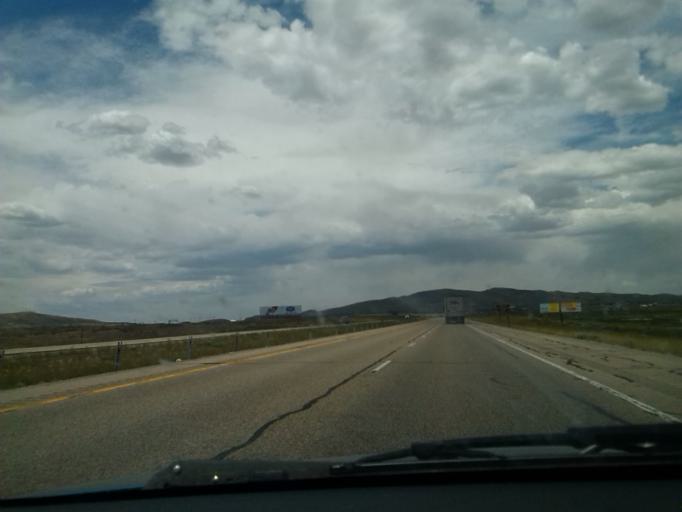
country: US
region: Wyoming
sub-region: Carbon County
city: Rawlins
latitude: 41.7859
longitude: -107.1795
